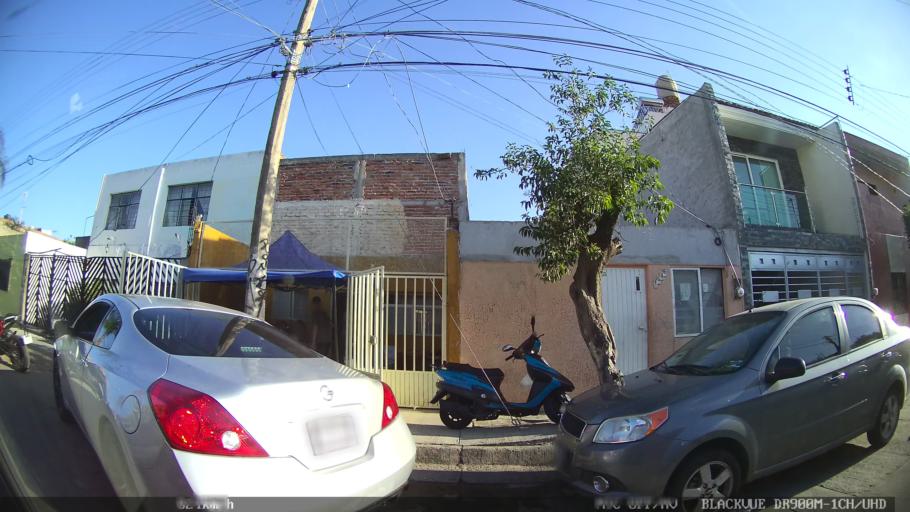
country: MX
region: Jalisco
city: Tlaquepaque
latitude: 20.6991
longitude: -103.2987
